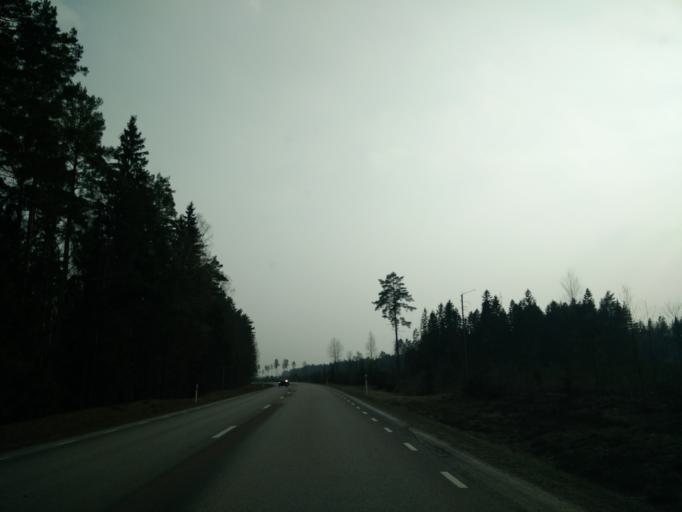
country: SE
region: Vaermland
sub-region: Forshaga Kommun
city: Forshaga
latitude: 59.5101
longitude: 13.4382
